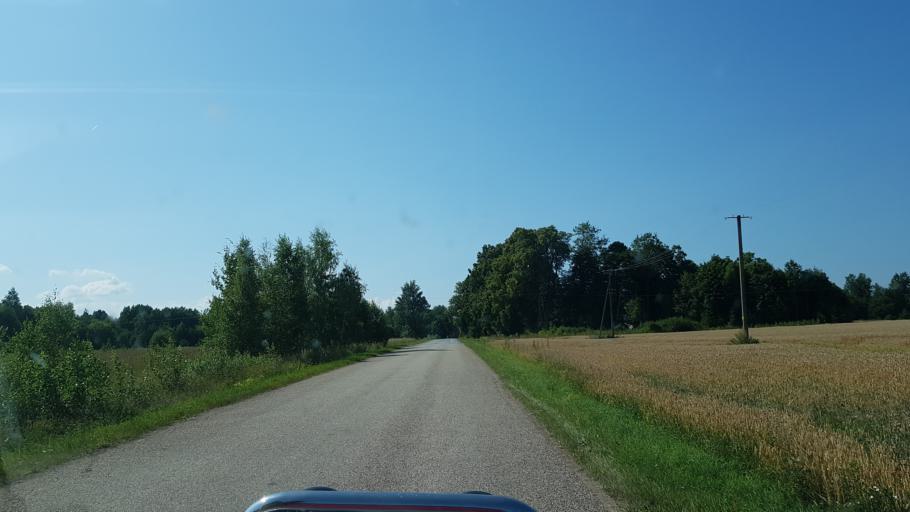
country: EE
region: Tartu
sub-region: Alatskivi vald
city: Kallaste
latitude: 58.6280
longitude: 27.0946
